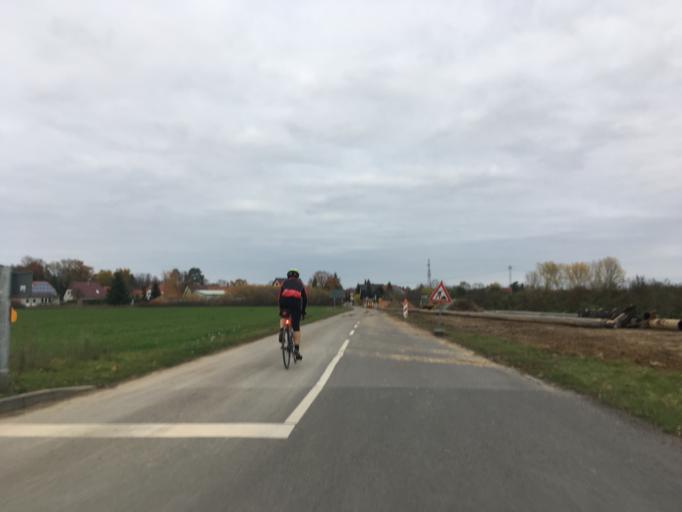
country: DE
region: Brandenburg
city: Frankfurt (Oder)
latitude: 52.3075
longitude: 14.5291
